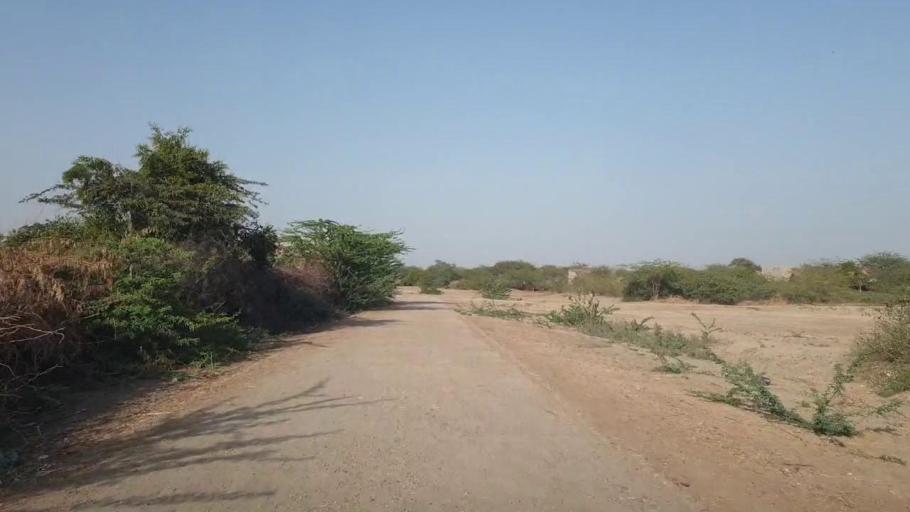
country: PK
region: Sindh
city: Dhoro Naro
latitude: 25.4718
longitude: 69.5626
